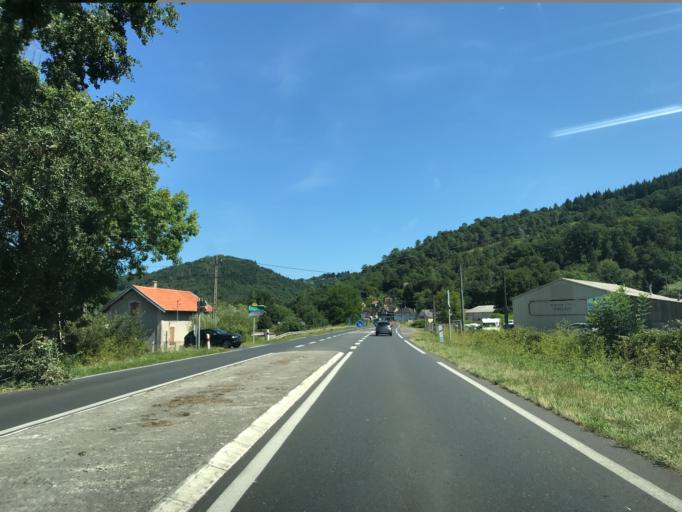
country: FR
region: Limousin
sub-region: Departement de la Correze
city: Cornil
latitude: 45.1951
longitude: 1.6567
